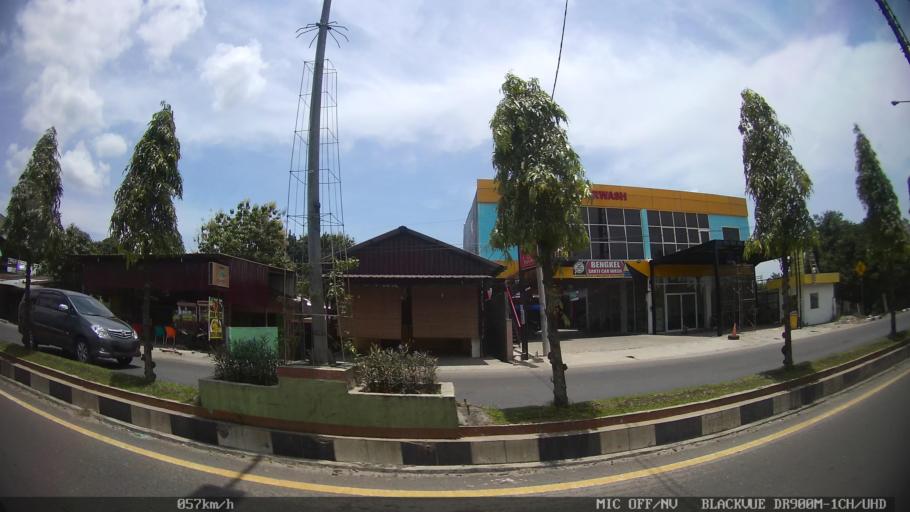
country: ID
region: North Sumatra
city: Binjai
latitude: 3.6075
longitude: 98.5214
